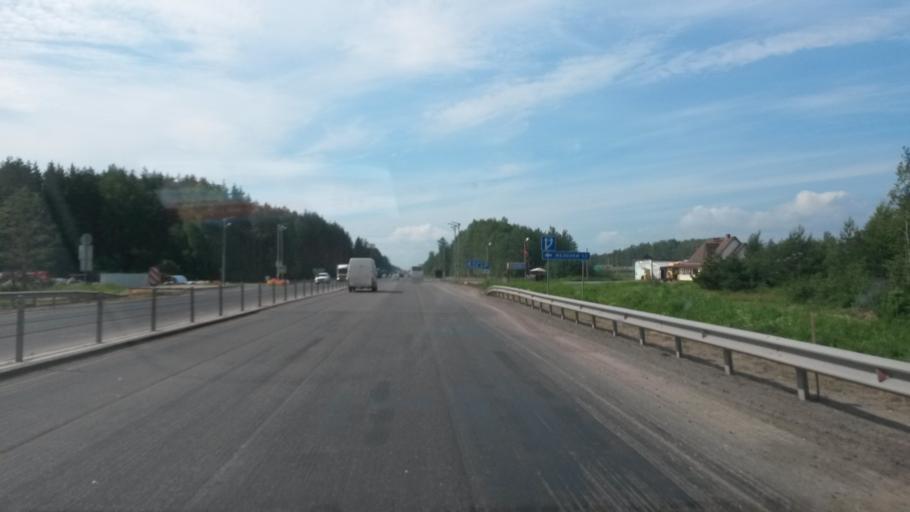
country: RU
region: Jaroslavl
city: Semibratovo
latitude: 57.2492
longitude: 39.4814
